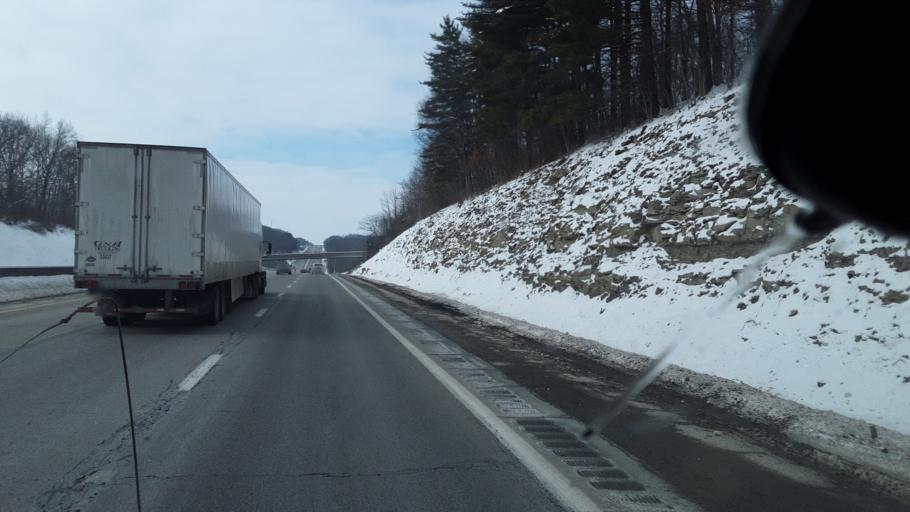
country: US
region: Ohio
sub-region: Perry County
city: Thornport
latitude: 39.9413
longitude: -82.3554
